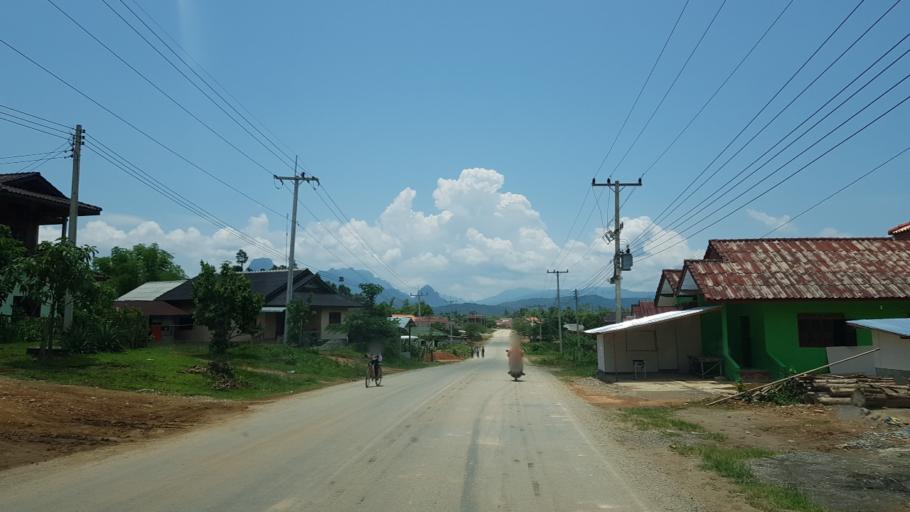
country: LA
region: Vientiane
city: Muang Kasi
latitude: 19.2705
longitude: 102.2270
